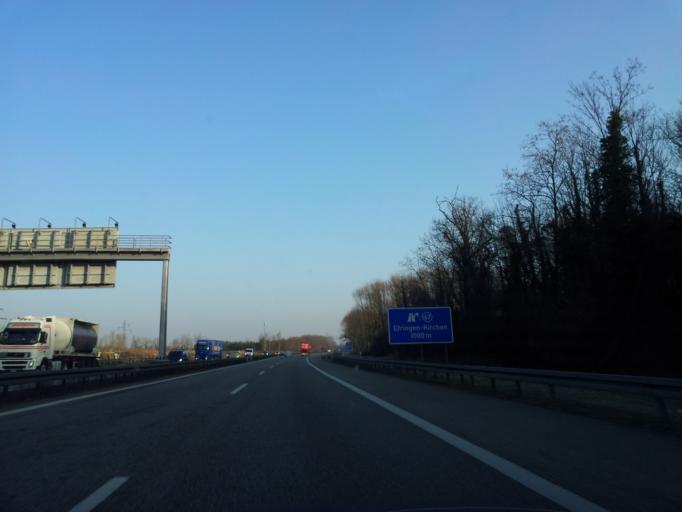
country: FR
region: Alsace
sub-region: Departement du Haut-Rhin
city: Kembs
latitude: 47.6666
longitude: 7.5248
